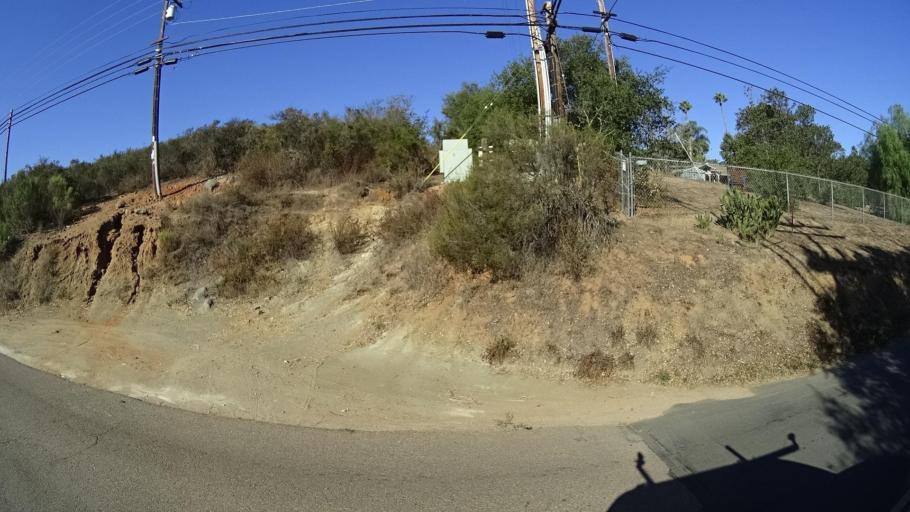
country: US
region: California
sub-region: San Diego County
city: Hidden Meadows
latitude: 33.2259
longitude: -117.1107
